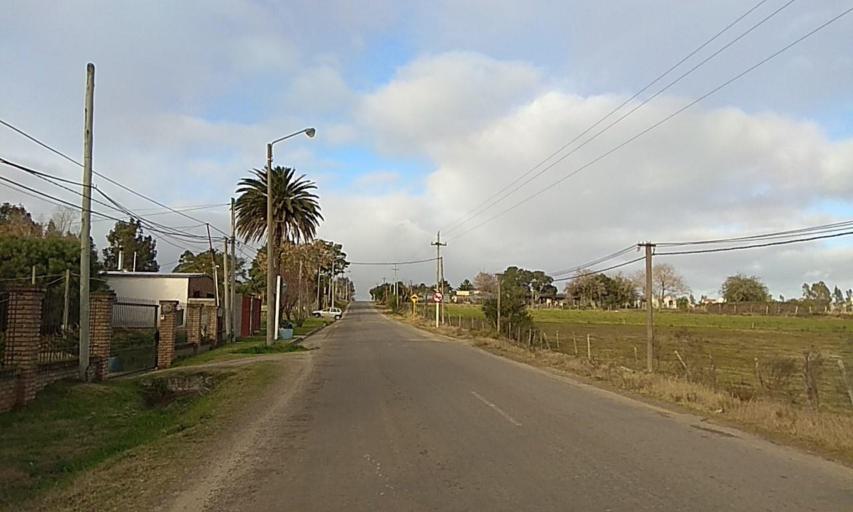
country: UY
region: Florida
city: Florida
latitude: -34.0804
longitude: -56.2117
